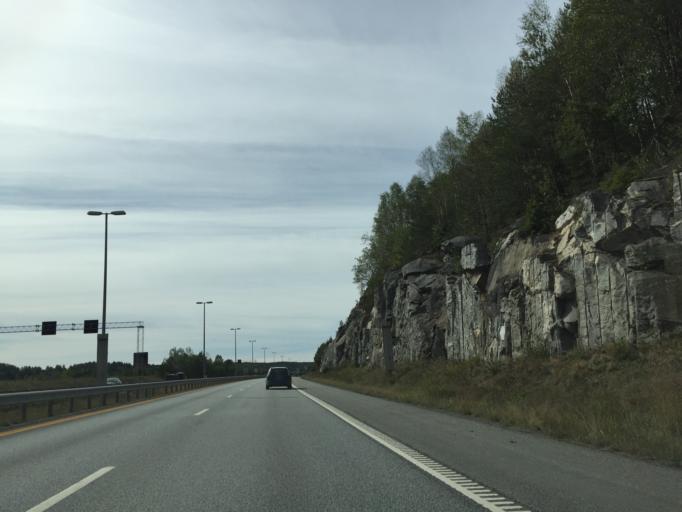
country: NO
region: Akershus
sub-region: Vestby
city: Vestby
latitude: 59.5249
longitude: 10.7294
